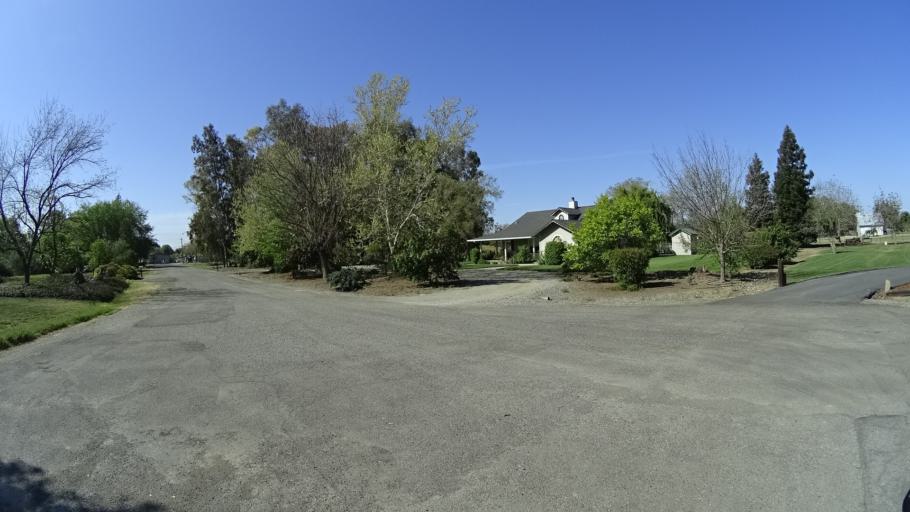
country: US
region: California
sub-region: Glenn County
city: Willows
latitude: 39.5348
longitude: -122.2042
